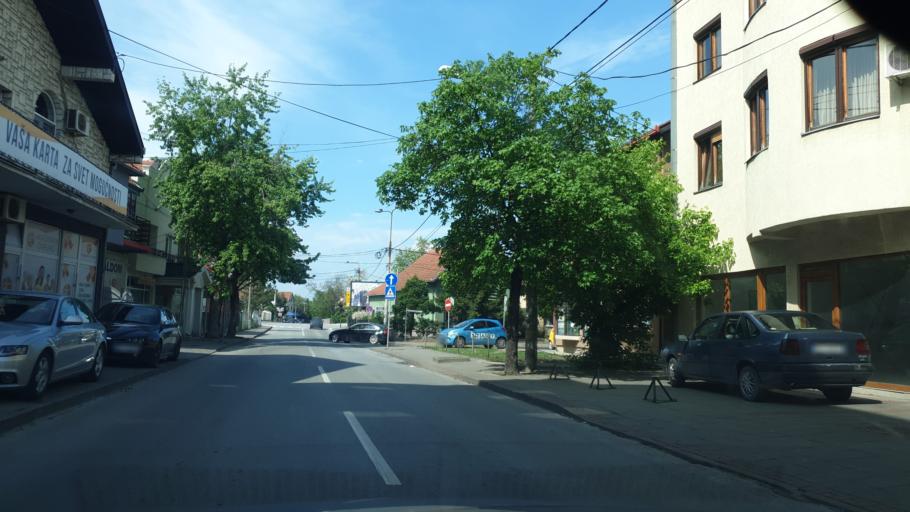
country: RS
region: Central Serbia
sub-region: Belgrade
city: Obrenovac
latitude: 44.6536
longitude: 20.1932
